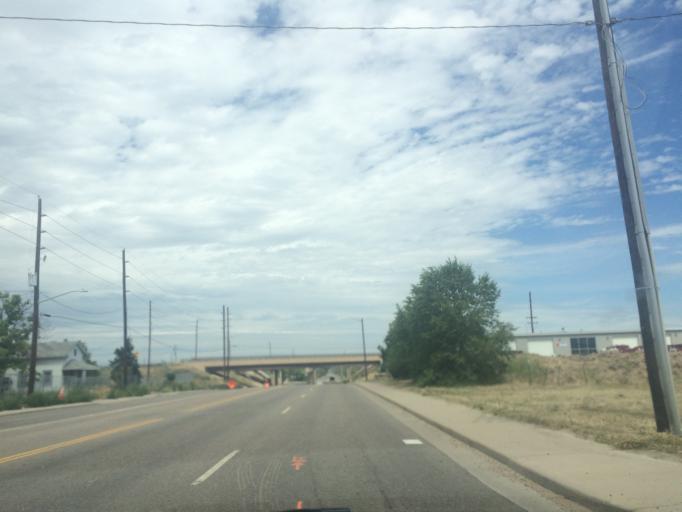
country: US
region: Colorado
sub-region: Adams County
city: Welby
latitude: 39.8223
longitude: -104.9591
